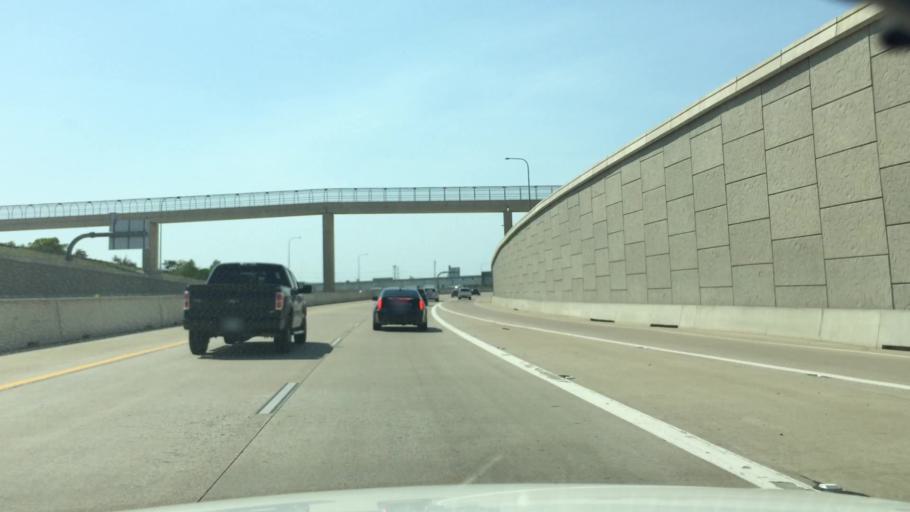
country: US
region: Texas
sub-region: Dallas County
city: Grand Prairie
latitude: 32.7479
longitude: -97.0252
